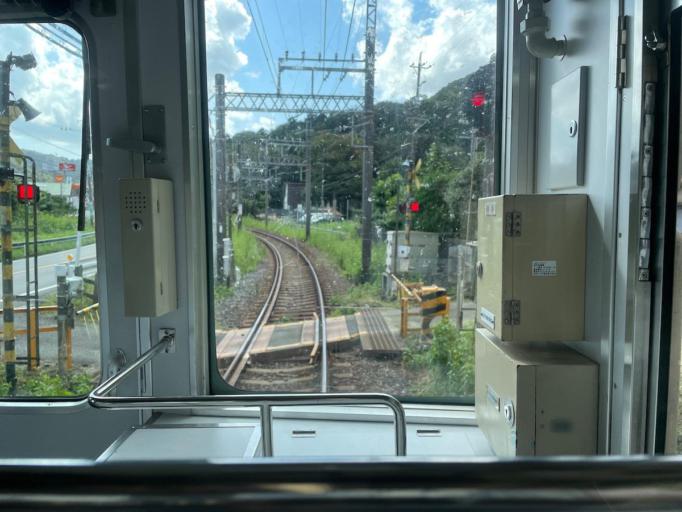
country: JP
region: Mie
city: Toba
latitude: 34.4635
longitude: 136.8396
